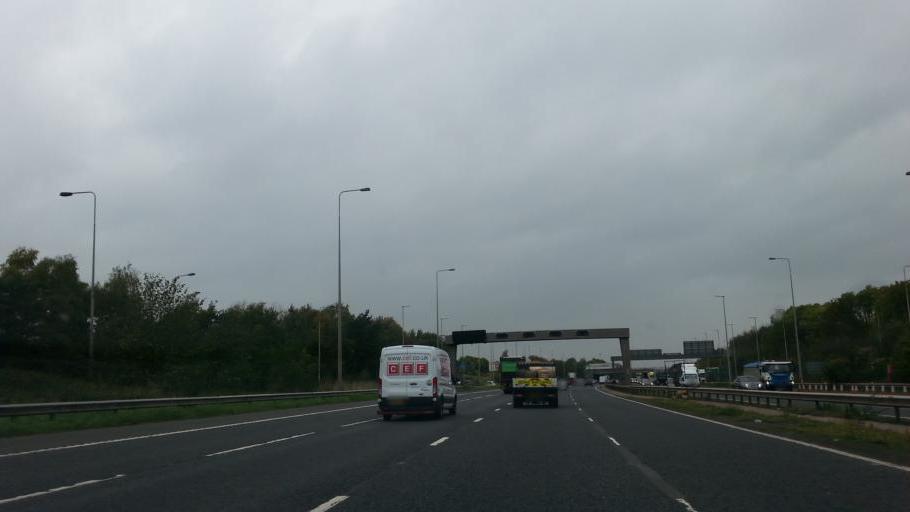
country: GB
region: England
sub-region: Warrington
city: Lymm
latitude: 53.3563
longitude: -2.5067
